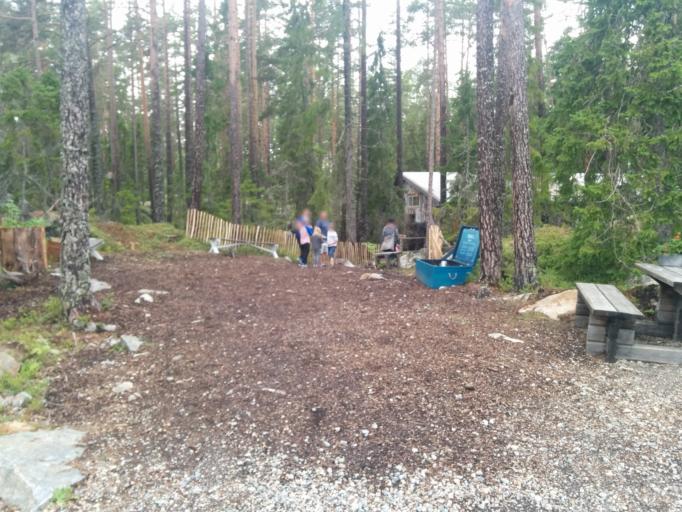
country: SE
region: Gaevleborg
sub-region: Nordanstigs Kommun
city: Bergsjoe
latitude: 61.9567
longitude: 17.3228
